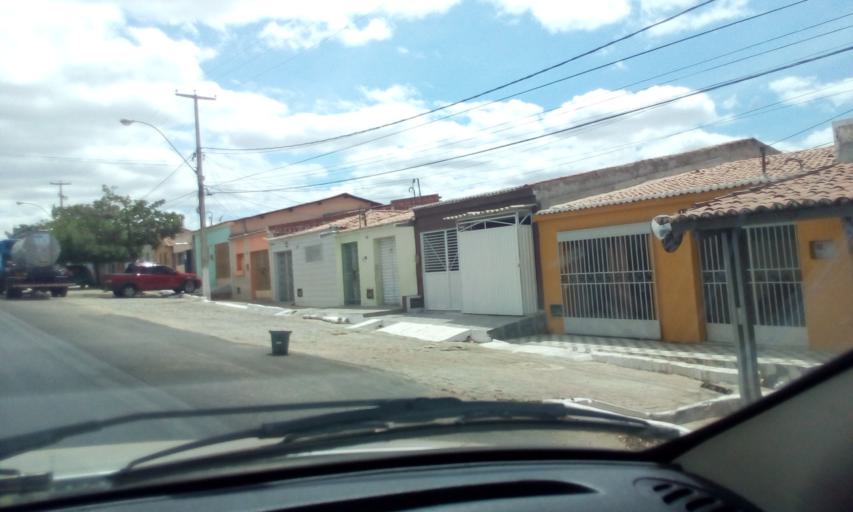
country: BR
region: Rio Grande do Norte
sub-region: Currais Novos
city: Currais Novos
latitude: -6.2581
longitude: -36.5063
